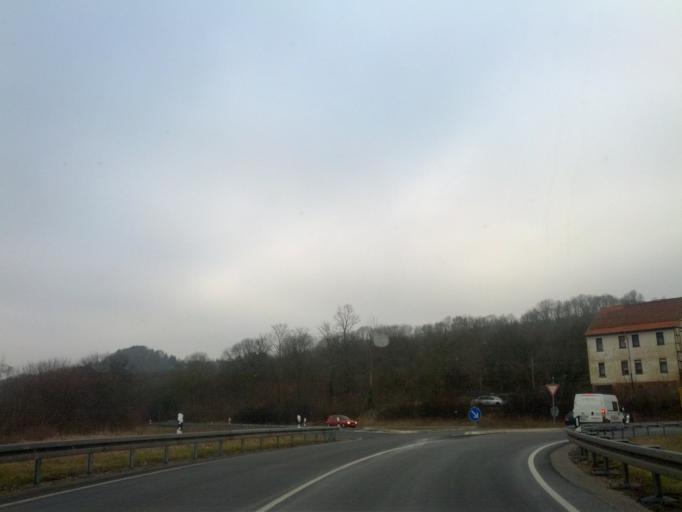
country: DE
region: Thuringia
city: Eisenach
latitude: 50.9796
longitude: 10.3561
